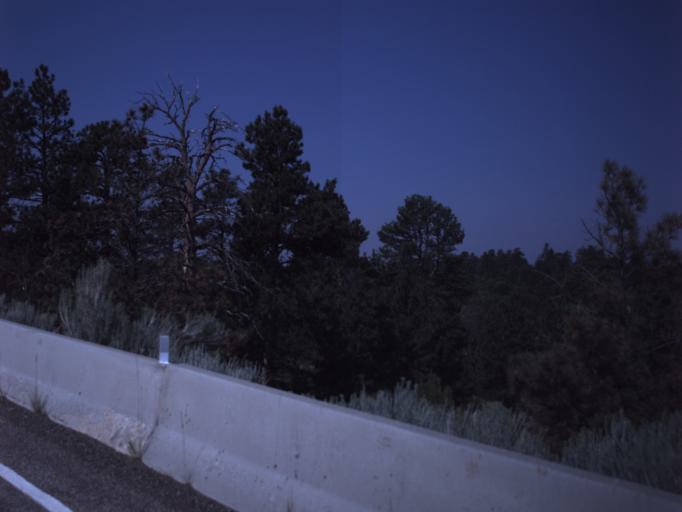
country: US
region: Utah
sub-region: Daggett County
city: Manila
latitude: 40.8947
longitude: -109.4579
